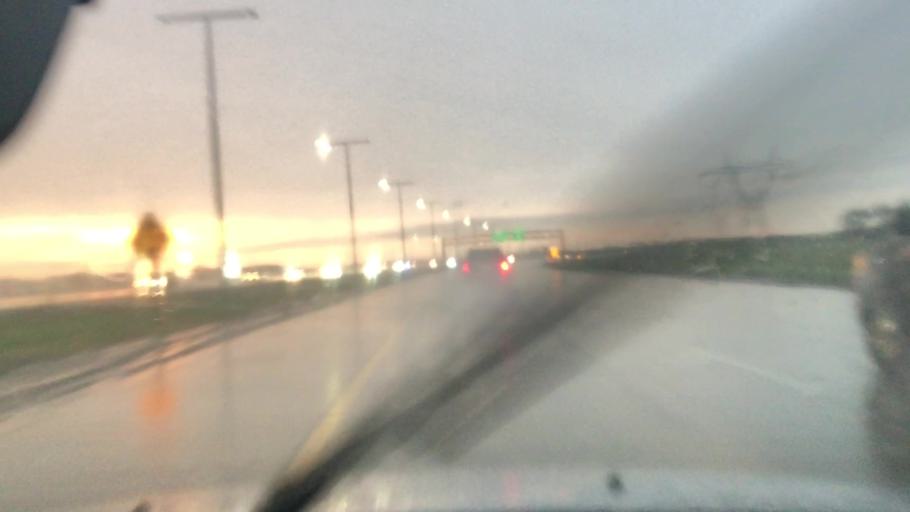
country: CA
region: Alberta
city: Devon
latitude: 53.4346
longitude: -113.5910
